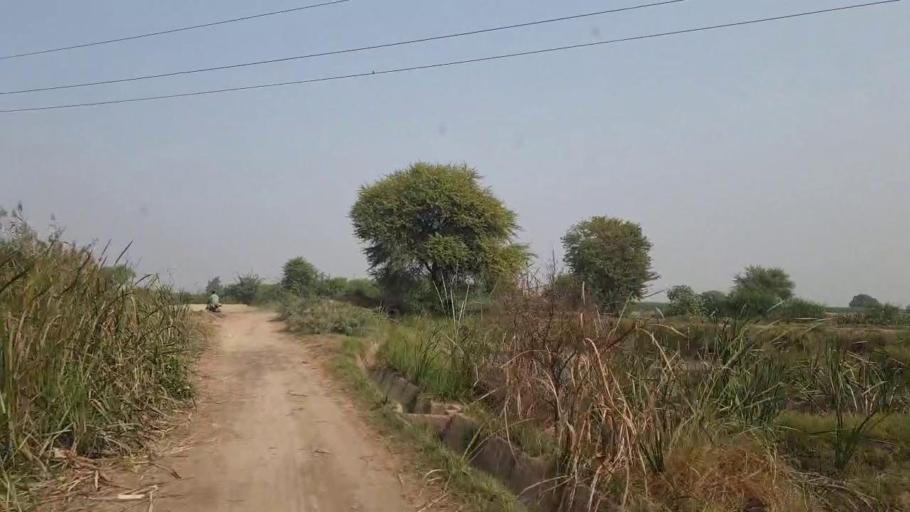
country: PK
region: Sindh
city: Matli
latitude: 25.0644
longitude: 68.6393
